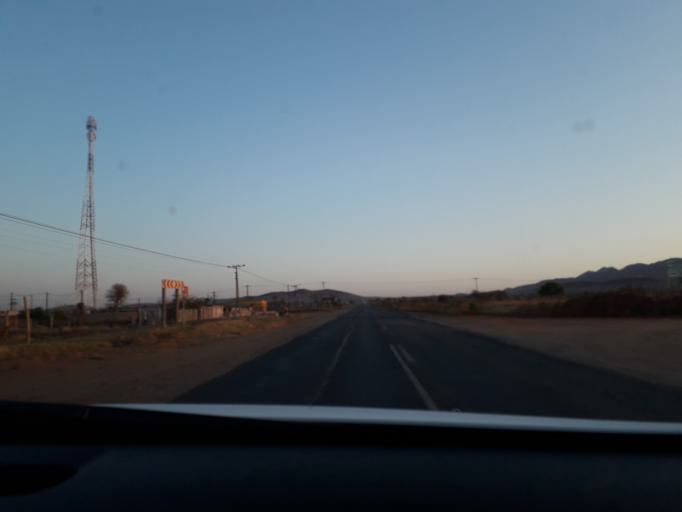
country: ZA
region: Limpopo
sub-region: Waterberg District Municipality
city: Mokopane
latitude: -24.0963
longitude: 28.9685
